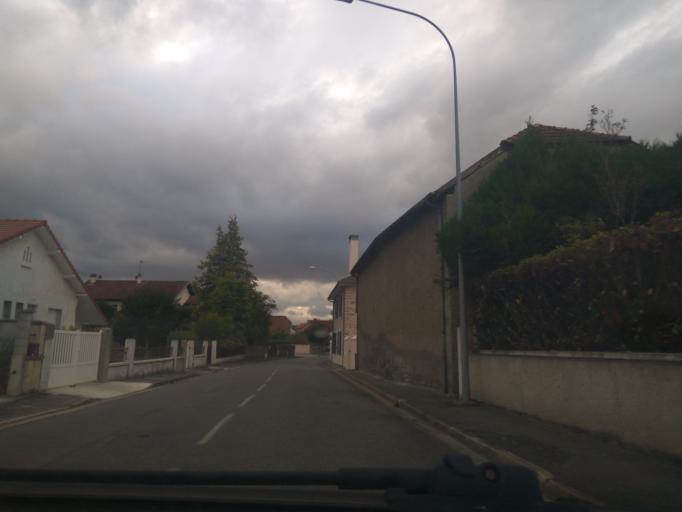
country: FR
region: Aquitaine
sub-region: Departement des Pyrenees-Atlantiques
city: Bizanos
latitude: 43.2876
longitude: -0.3482
